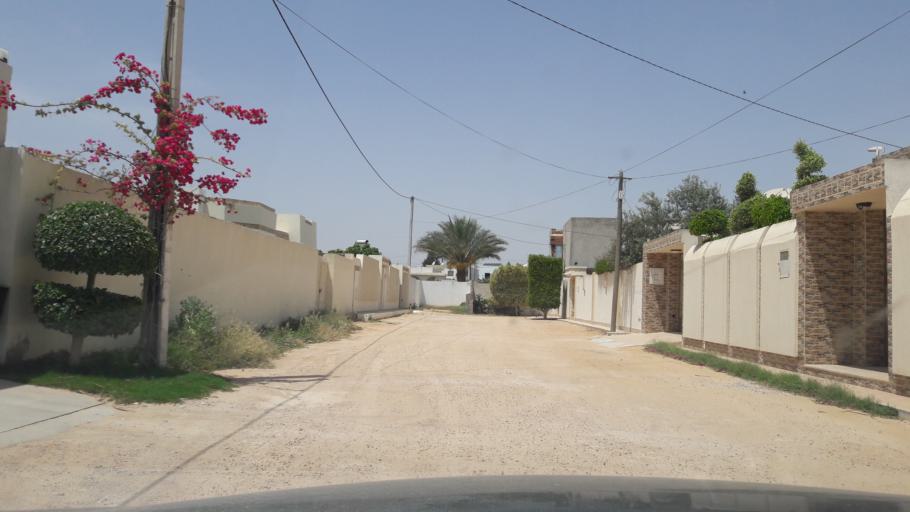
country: TN
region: Safaqis
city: Sfax
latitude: 34.7798
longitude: 10.7558
